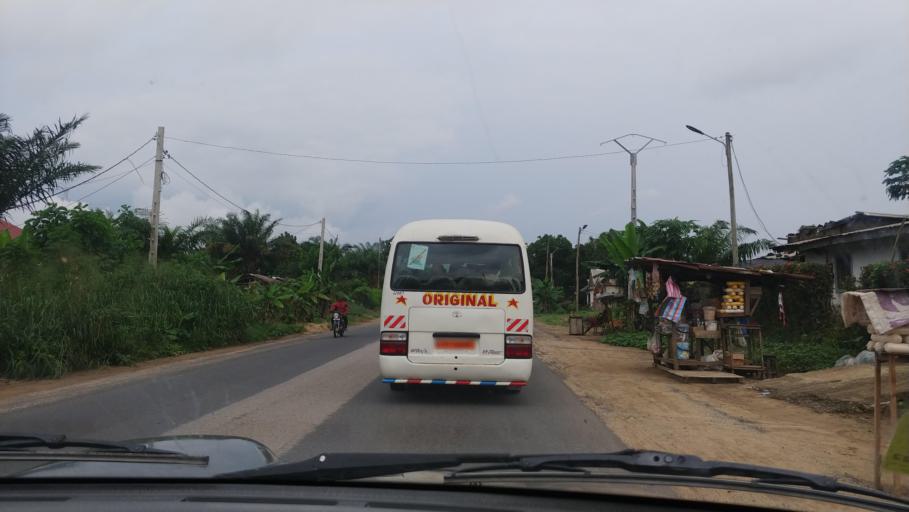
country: CM
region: Littoral
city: Dibombari
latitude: 4.1496
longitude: 9.5880
